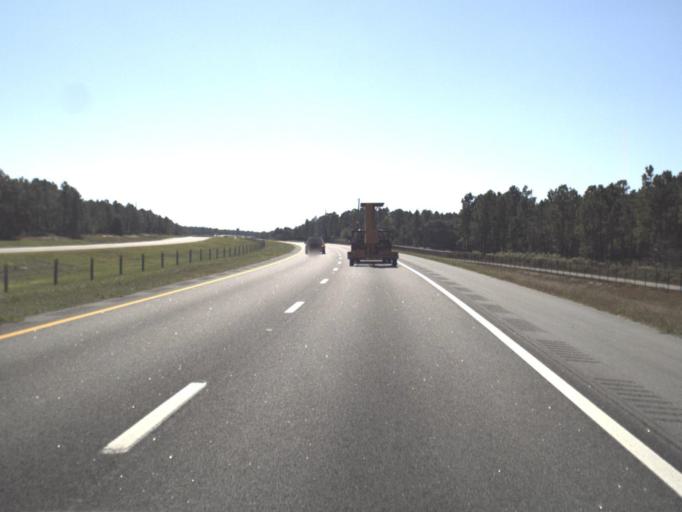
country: US
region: Florida
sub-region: Pasco County
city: Shady Hills
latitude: 28.3671
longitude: -82.5451
